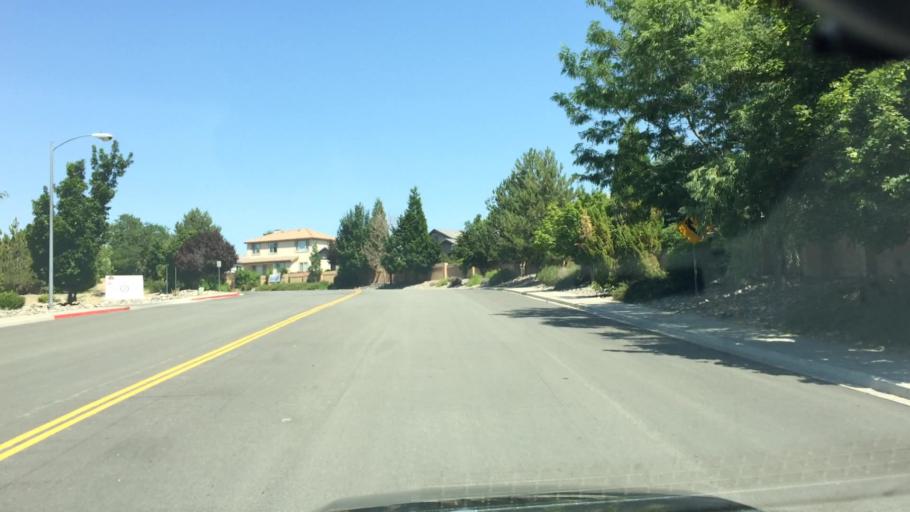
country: US
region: Nevada
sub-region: Washoe County
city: Sparks
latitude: 39.5766
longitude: -119.7184
